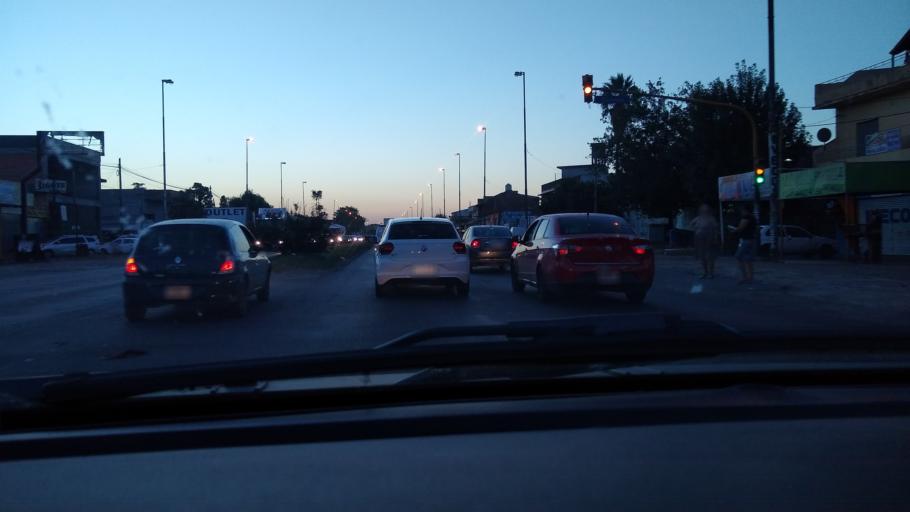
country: AR
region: Buenos Aires
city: San Justo
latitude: -34.6810
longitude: -58.5776
